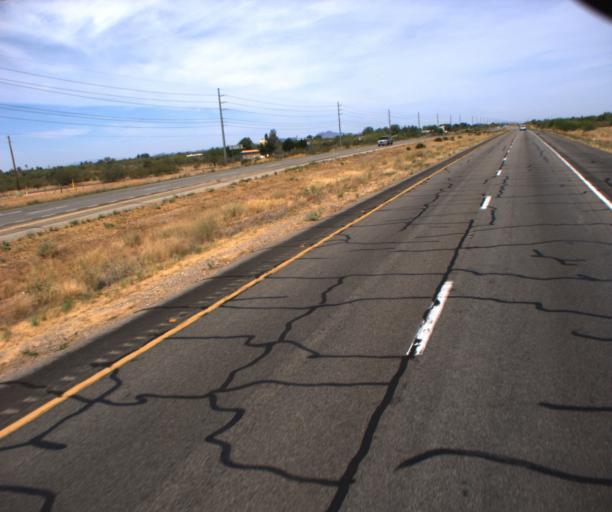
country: US
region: Arizona
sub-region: Maricopa County
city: Sun City West
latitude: 33.7675
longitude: -112.5152
